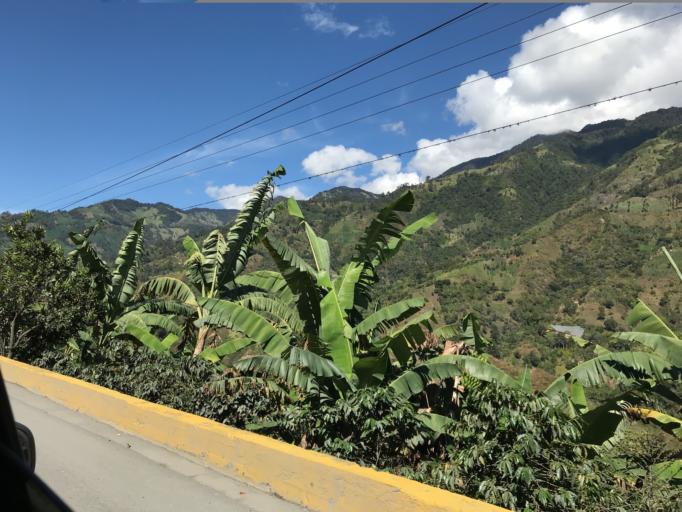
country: CO
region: Tolima
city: Cajamarca
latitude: 4.4423
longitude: -75.4167
